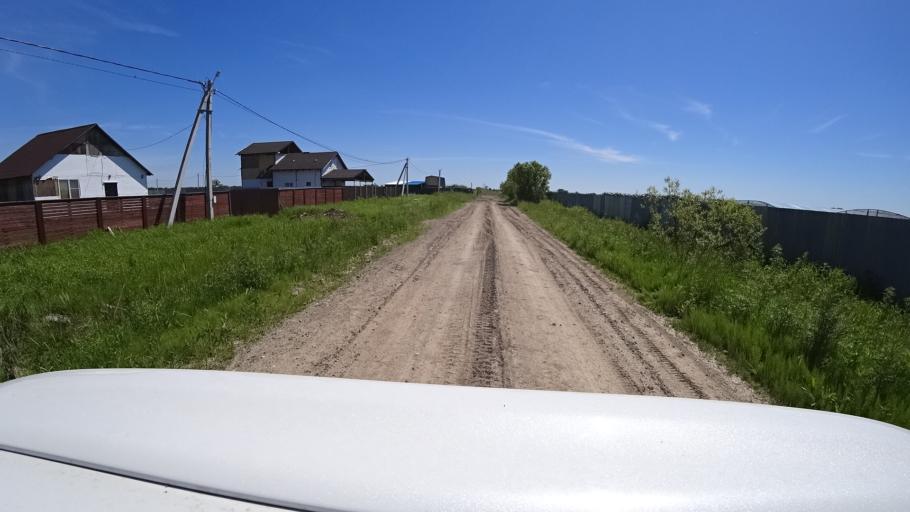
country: RU
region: Khabarovsk Krai
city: Topolevo
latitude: 48.5096
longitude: 135.2031
